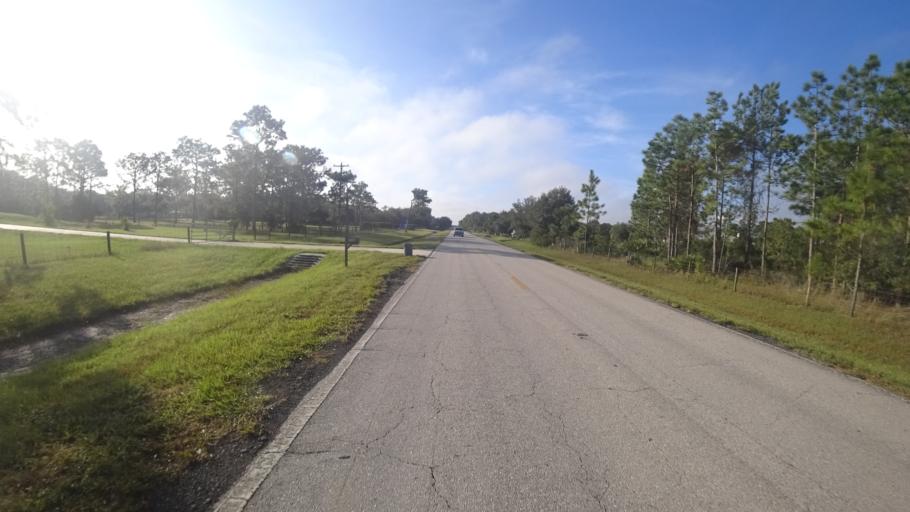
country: US
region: Florida
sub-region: Sarasota County
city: The Meadows
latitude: 27.4113
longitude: -82.3038
